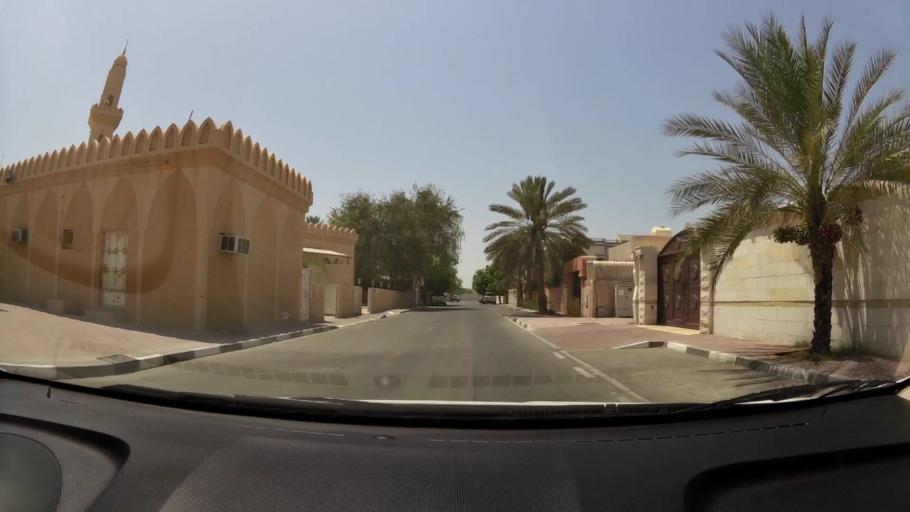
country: AE
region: Ash Shariqah
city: Sharjah
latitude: 25.2926
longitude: 55.3445
